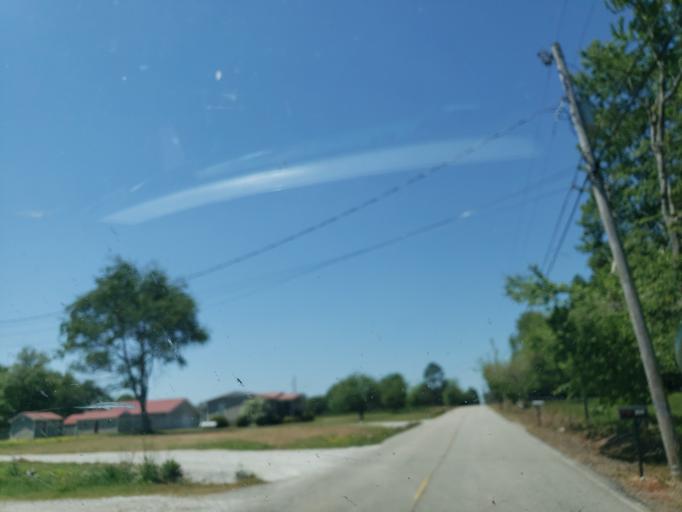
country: US
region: Alabama
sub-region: Madison County
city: Hazel Green
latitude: 34.9620
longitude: -86.6361
